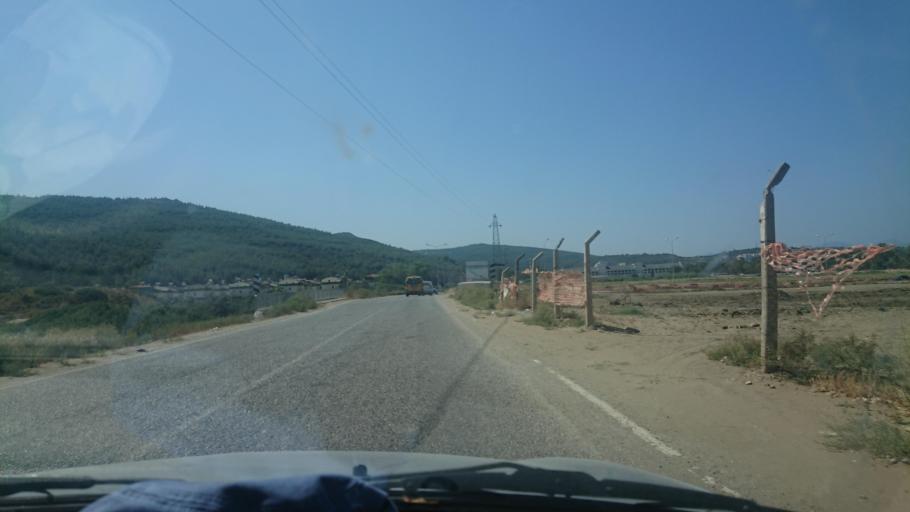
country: TR
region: Izmir
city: Selcuk
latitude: 37.9432
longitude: 27.2798
